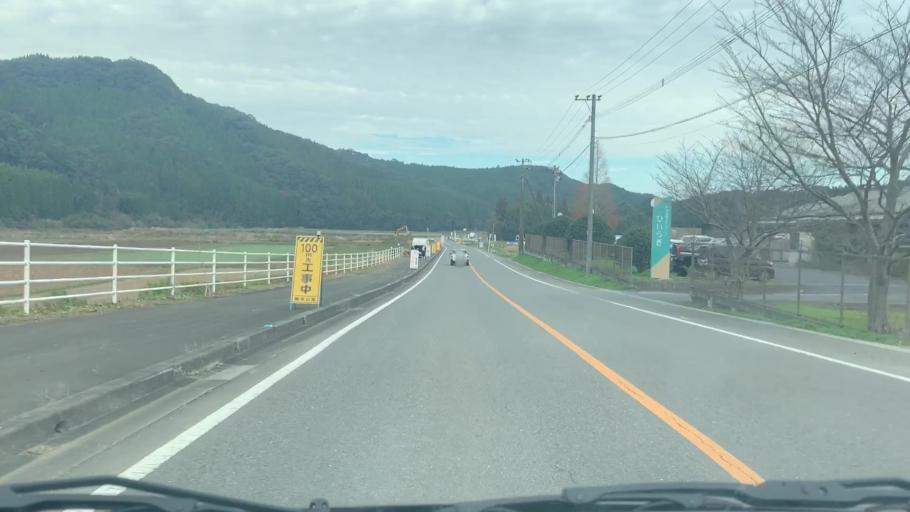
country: JP
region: Saga Prefecture
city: Takeocho-takeo
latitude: 33.2450
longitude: 129.9698
